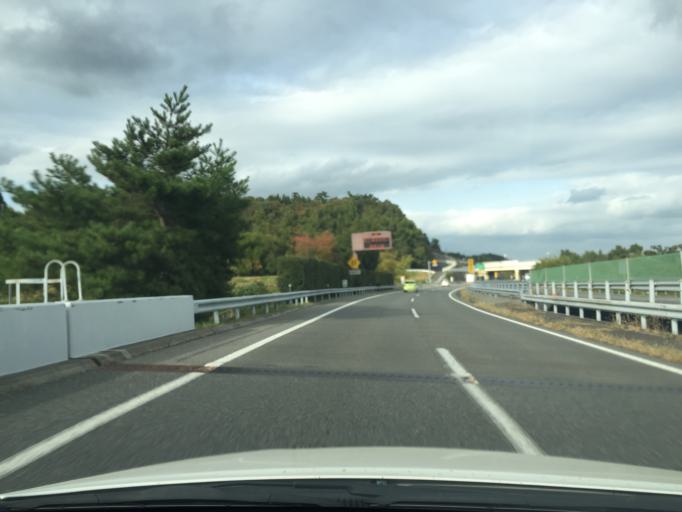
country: JP
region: Fukushima
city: Iwaki
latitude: 37.0620
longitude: 140.8324
